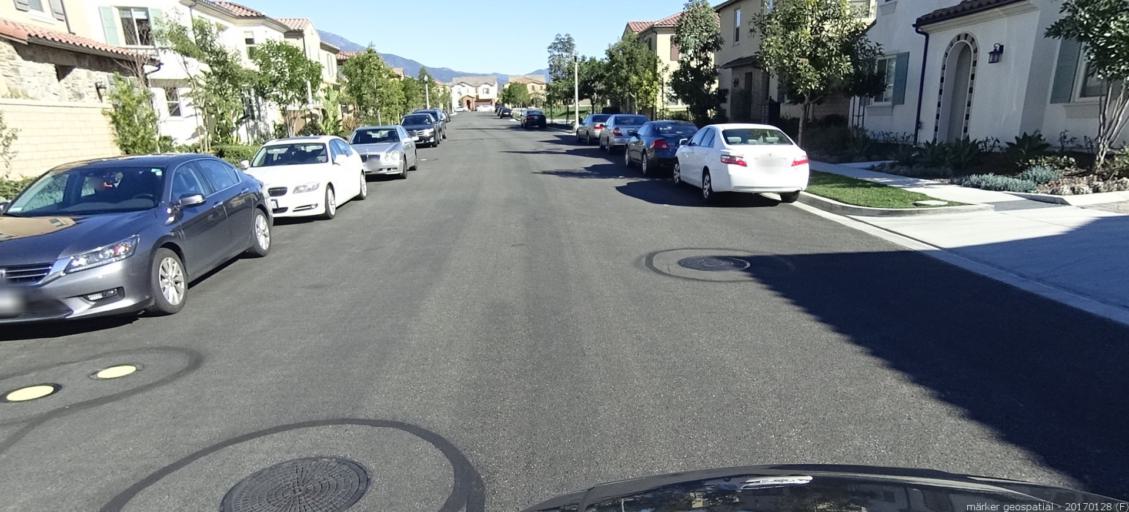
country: US
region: California
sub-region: Orange County
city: Lake Forest
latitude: 33.6687
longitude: -117.6804
